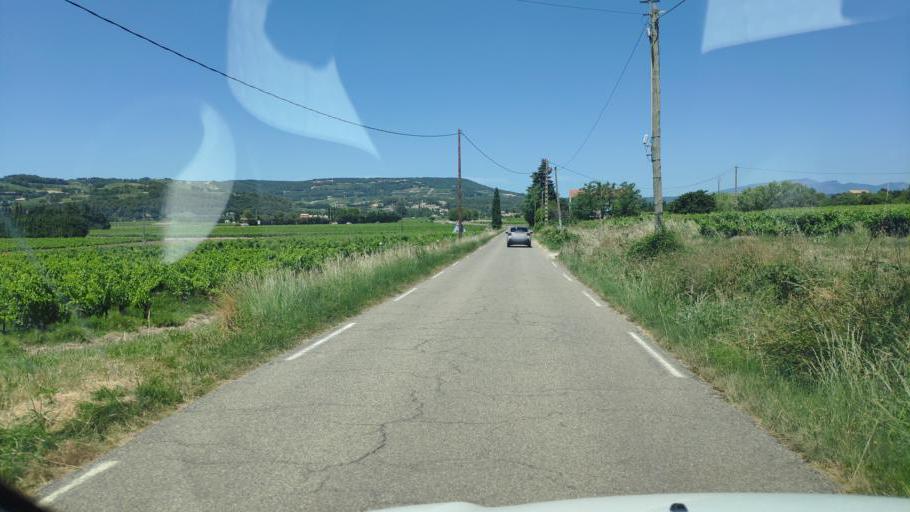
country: FR
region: Provence-Alpes-Cote d'Azur
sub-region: Departement du Vaucluse
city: Sablet
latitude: 44.2281
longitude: 5.0186
